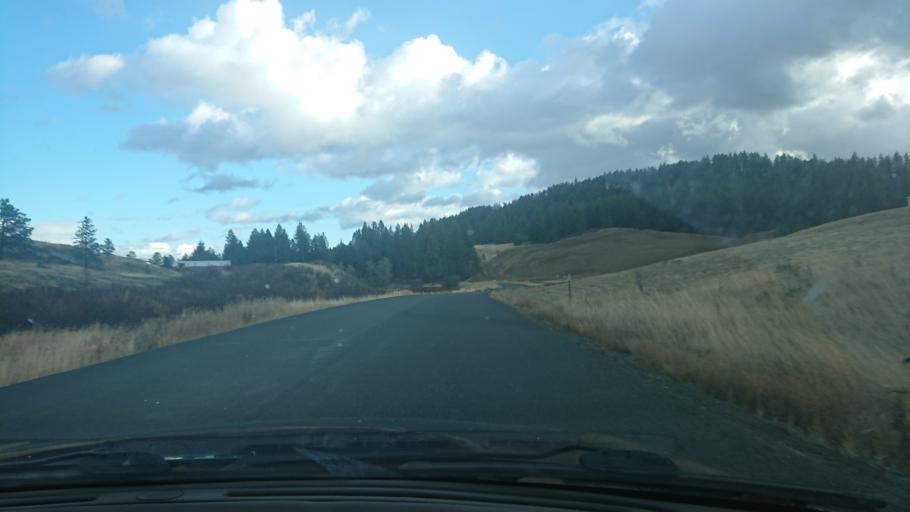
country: US
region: Idaho
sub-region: Latah County
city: Moscow
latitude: 46.7030
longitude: -116.8630
